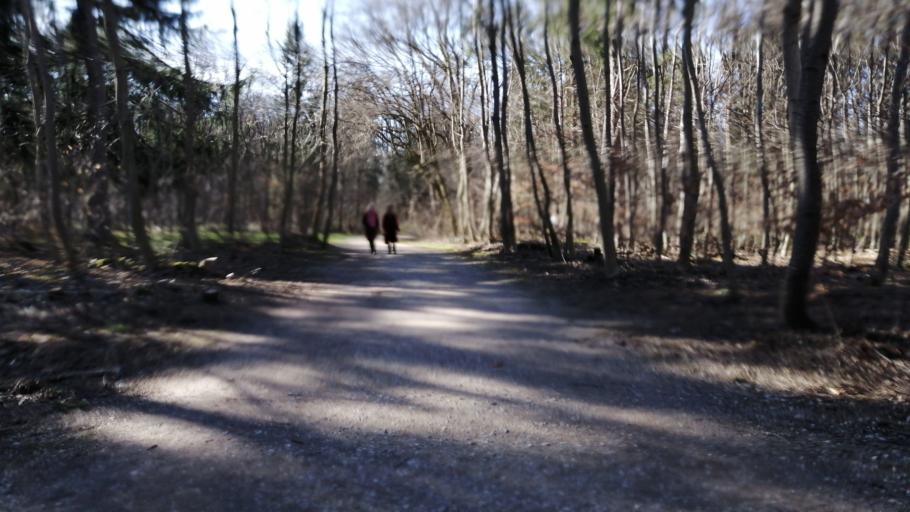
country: DE
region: Bavaria
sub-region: Upper Bavaria
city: Pullach im Isartal
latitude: 48.1052
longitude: 11.5137
